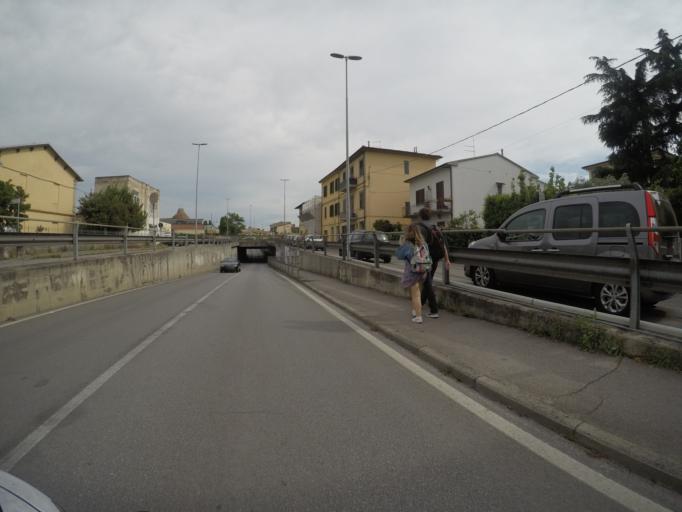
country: IT
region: Tuscany
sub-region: Province of Pisa
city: Madonna dell'Acqua
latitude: 43.7266
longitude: 10.3900
